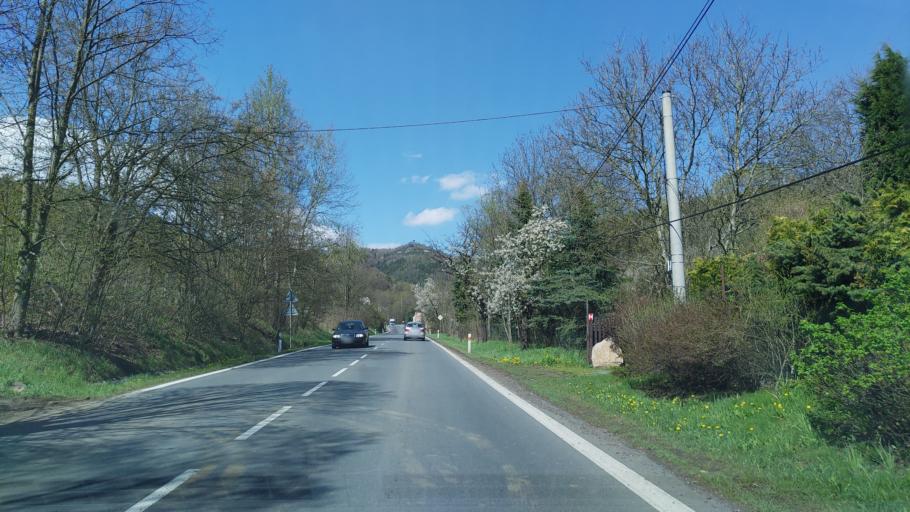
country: CZ
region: Ustecky
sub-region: Okres Chomutov
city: Perstejn
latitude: 50.3627
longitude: 13.0836
